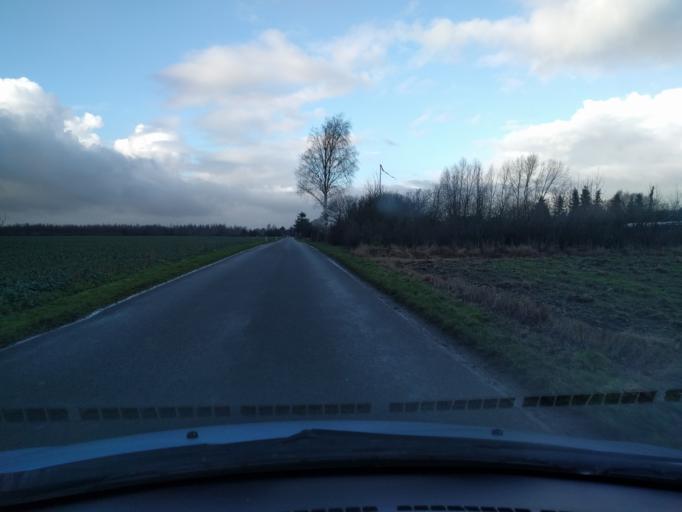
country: DK
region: South Denmark
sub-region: Kerteminde Kommune
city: Langeskov
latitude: 55.3910
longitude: 10.5698
